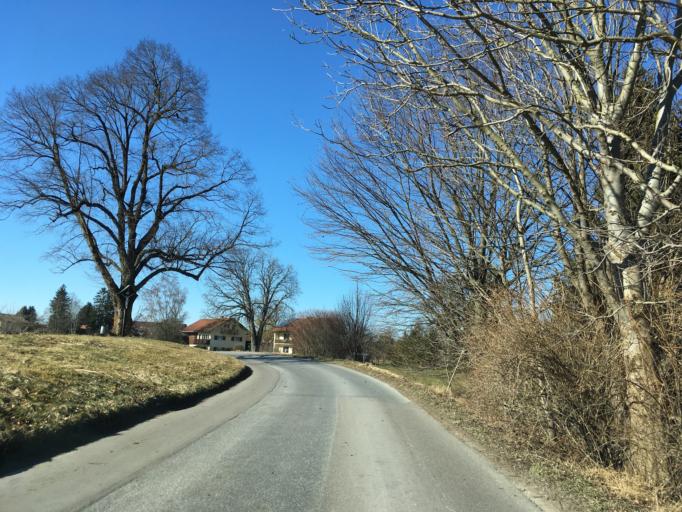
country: DE
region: Bavaria
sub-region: Upper Bavaria
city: Bad Aibling
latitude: 47.8527
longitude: 11.9936
